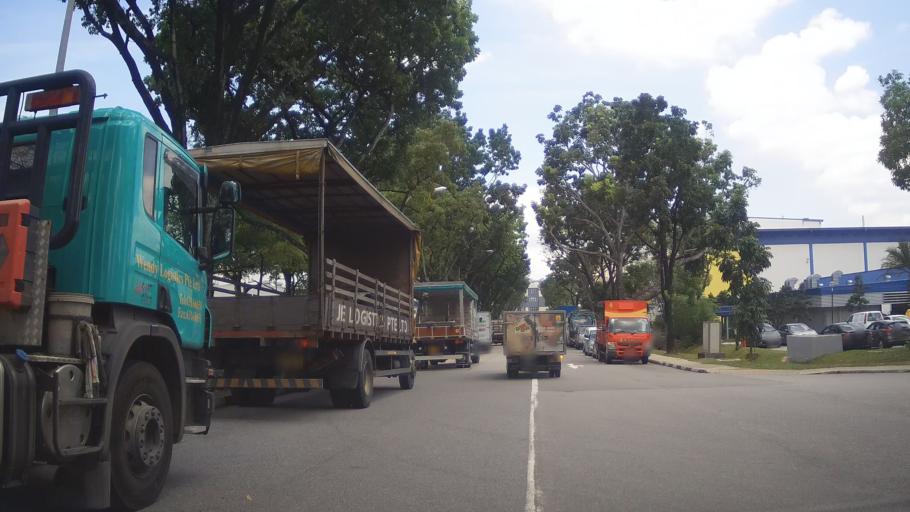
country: MY
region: Johor
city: Johor Bahru
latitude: 1.3327
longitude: 103.7100
